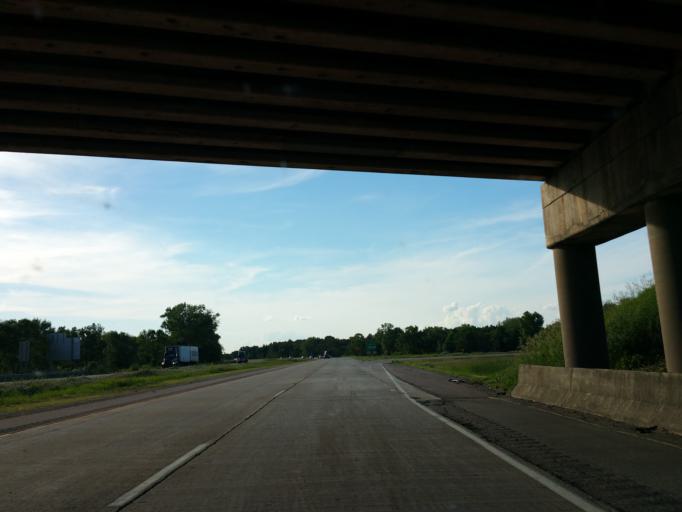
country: US
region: Wisconsin
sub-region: Columbia County
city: Portage
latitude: 43.5133
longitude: -89.5233
